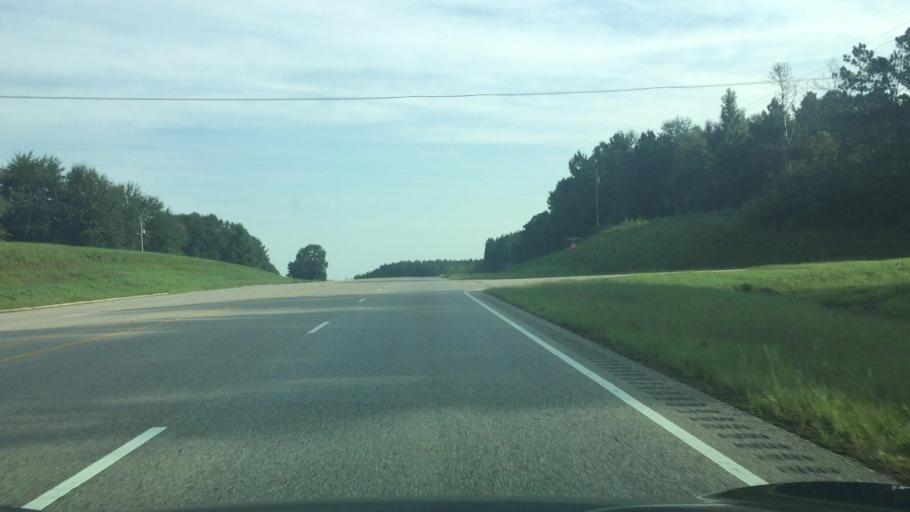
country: US
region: Alabama
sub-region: Covington County
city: Andalusia
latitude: 31.4344
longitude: -86.6117
